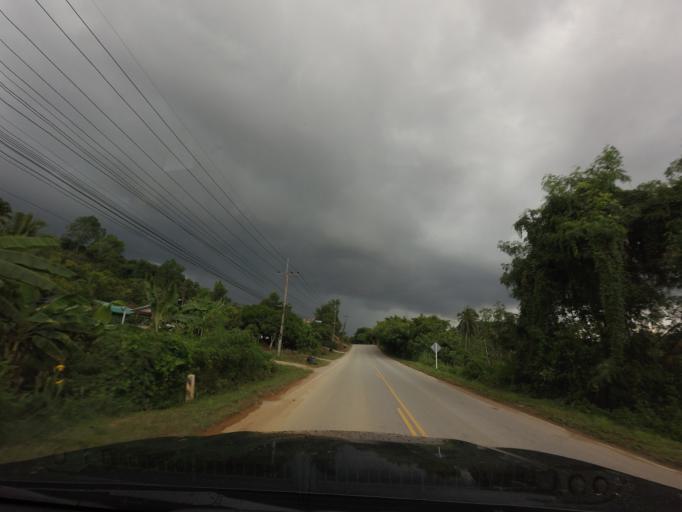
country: LA
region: Vientiane
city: Muang Sanakham
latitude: 17.9537
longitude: 101.7405
